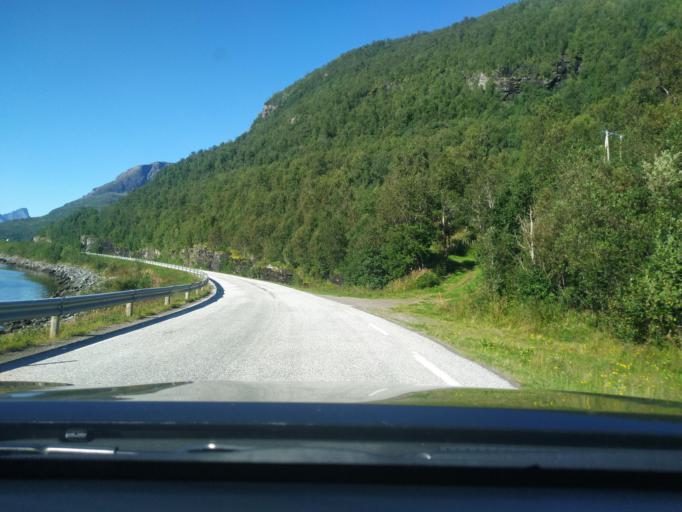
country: NO
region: Troms
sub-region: Dyroy
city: Brostadbotn
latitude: 68.9343
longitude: 17.6990
